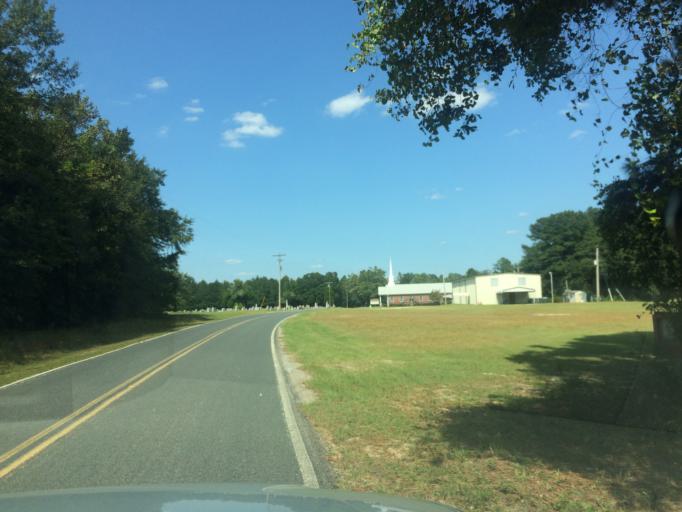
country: US
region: South Carolina
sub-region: Barnwell County
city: Williston
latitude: 33.6440
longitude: -81.4408
